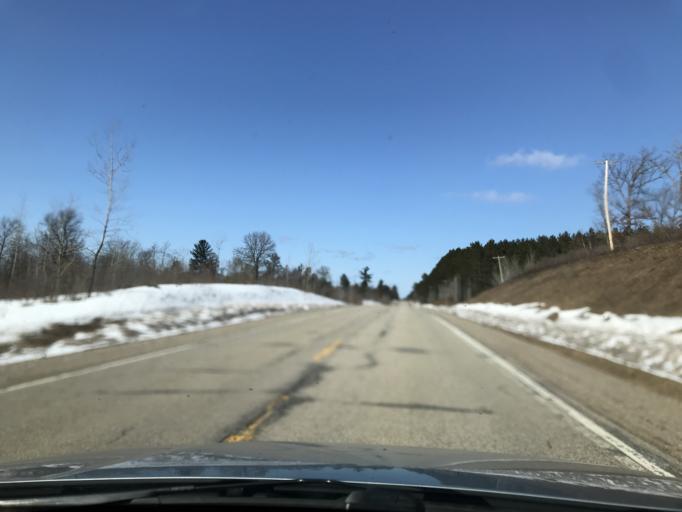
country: US
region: Wisconsin
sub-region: Marinette County
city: Niagara
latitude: 45.3768
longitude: -88.1000
